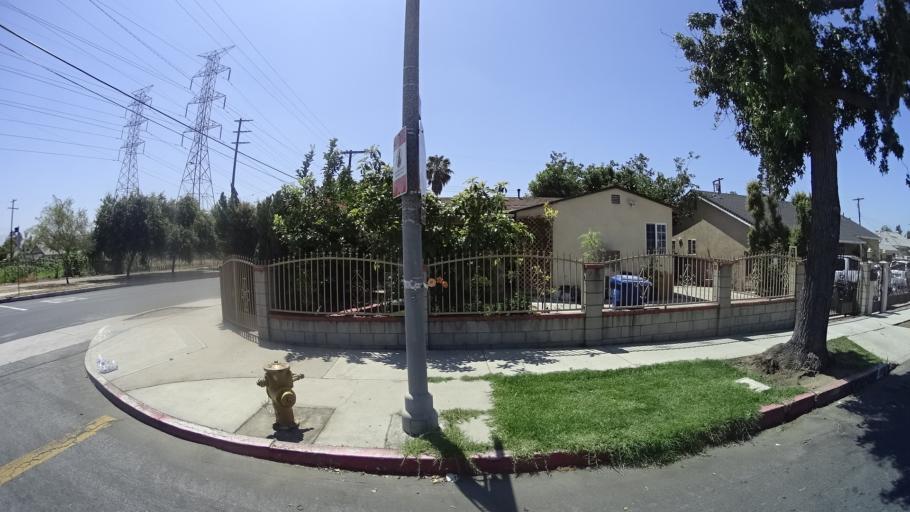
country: US
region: California
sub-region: Los Angeles County
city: Van Nuys
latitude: 34.2324
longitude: -118.4277
